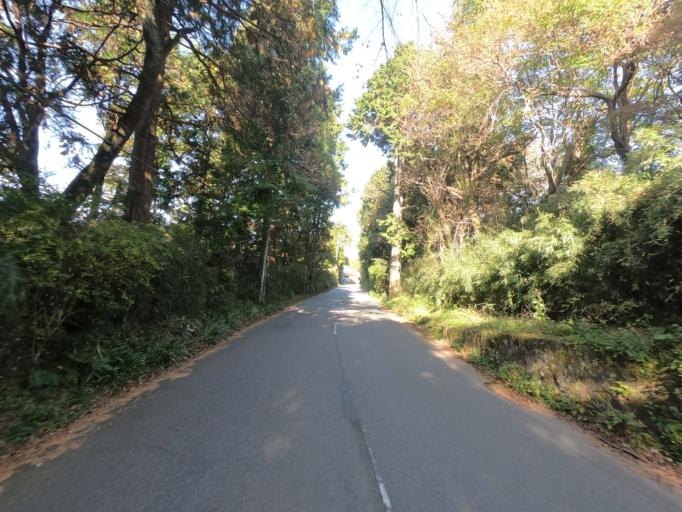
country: JP
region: Kanagawa
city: Hakone
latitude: 35.2053
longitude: 139.0187
